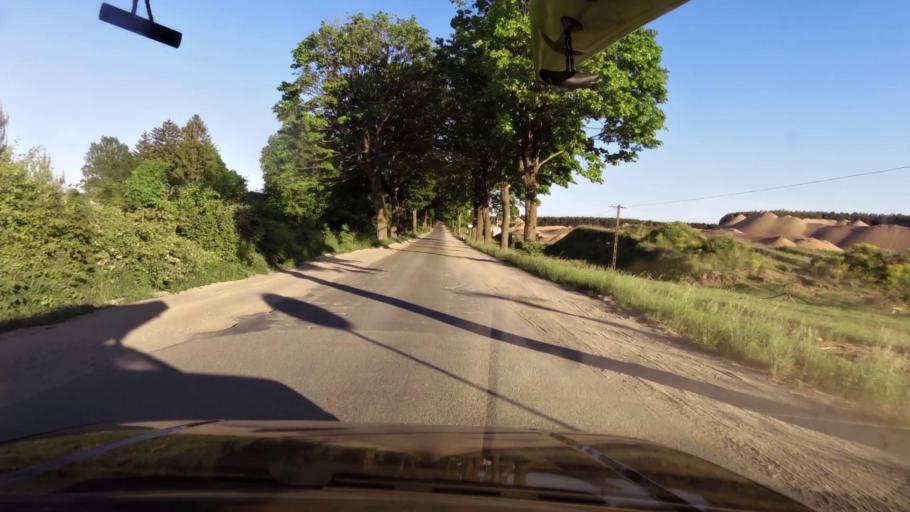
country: PL
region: West Pomeranian Voivodeship
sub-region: Powiat szczecinecki
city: Bialy Bor
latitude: 53.9385
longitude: 16.7905
